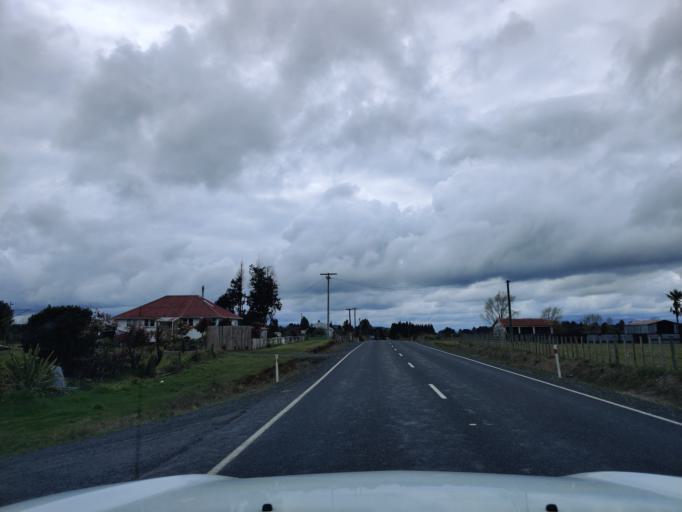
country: NZ
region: Waikato
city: Turangi
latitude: -39.0072
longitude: 175.3772
